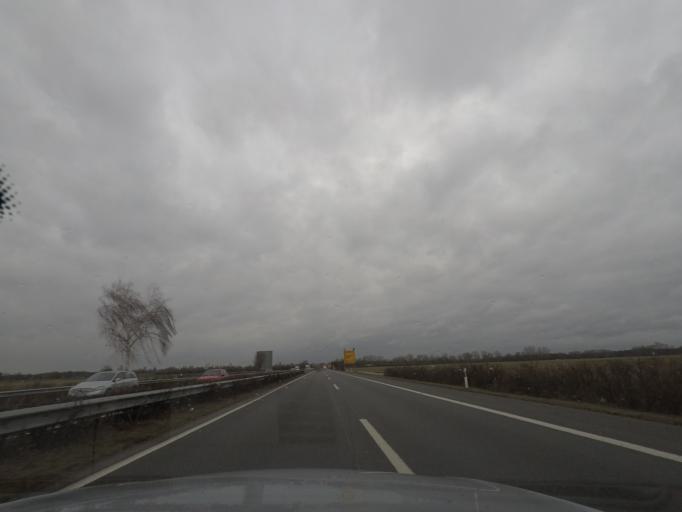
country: DE
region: Rheinland-Pfalz
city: Waldsee
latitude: 49.3949
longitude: 8.4141
